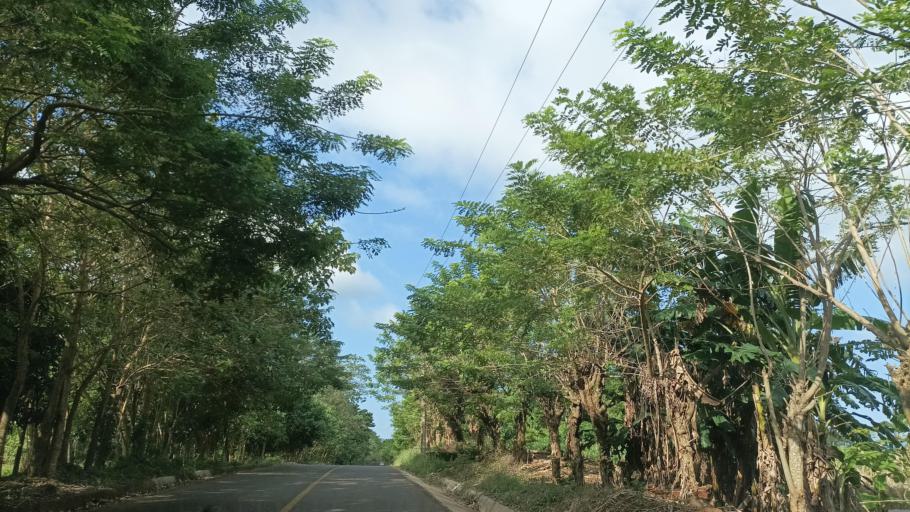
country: MX
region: Veracruz
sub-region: Pajapan
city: Pajapan
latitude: 18.1858
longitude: -94.6830
